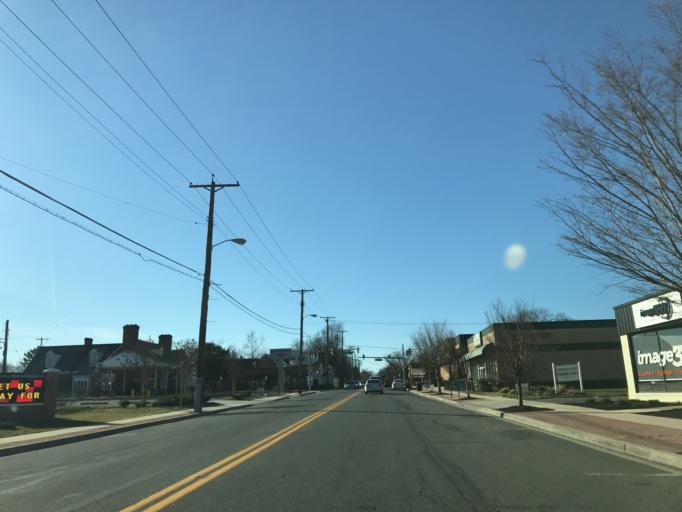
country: US
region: Maryland
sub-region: Harford County
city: Aberdeen
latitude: 39.5100
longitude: -76.1657
